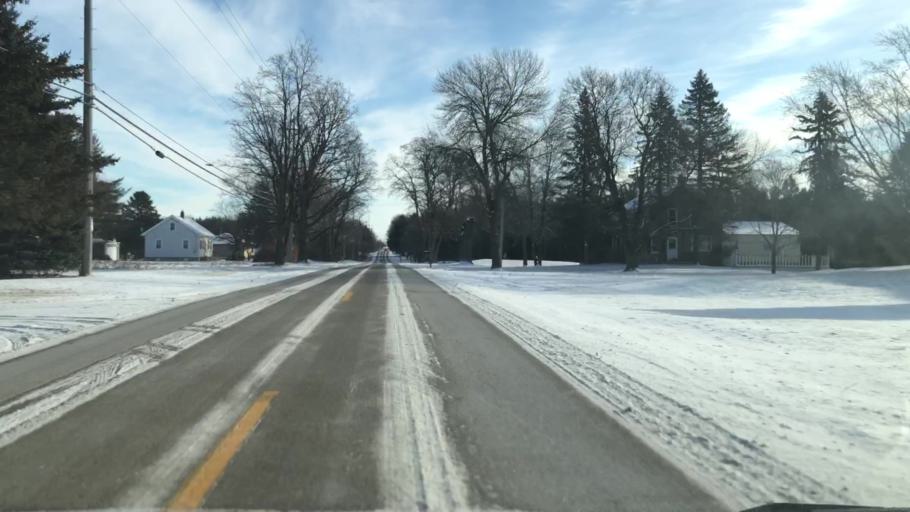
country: US
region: Wisconsin
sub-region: Waukesha County
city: Lannon
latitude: 43.1700
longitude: -88.1767
